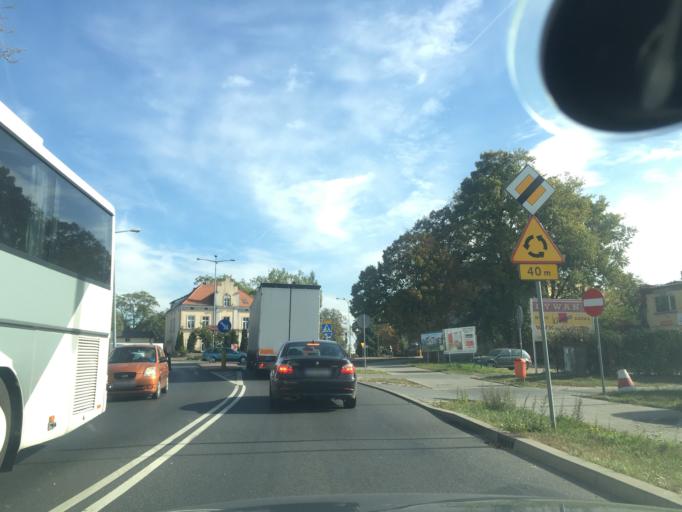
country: PL
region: Greater Poland Voivodeship
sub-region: Powiat wrzesinski
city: Wrzesnia
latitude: 52.3292
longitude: 17.5623
